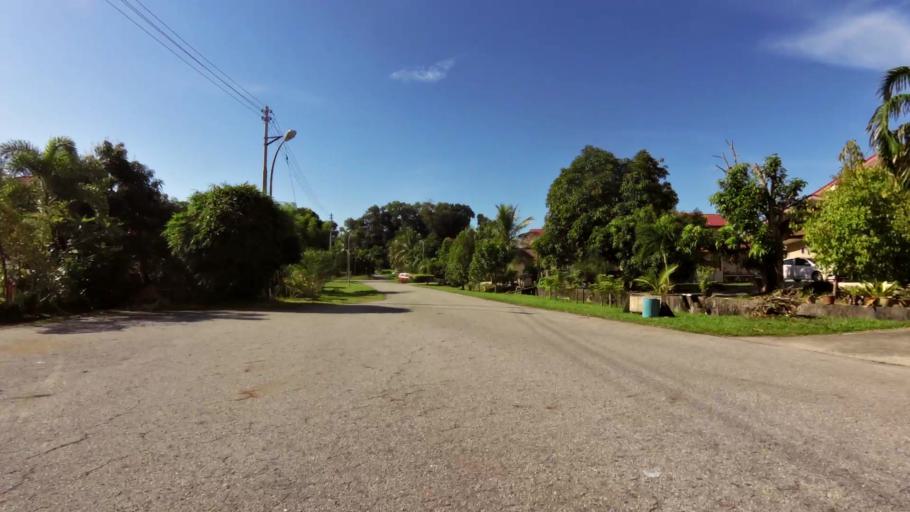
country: BN
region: Brunei and Muara
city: Bandar Seri Begawan
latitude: 4.9788
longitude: 114.9585
